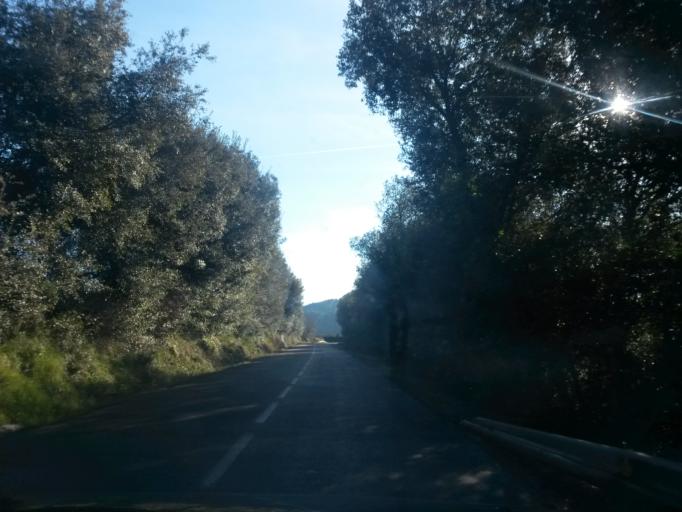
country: ES
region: Catalonia
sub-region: Provincia de Girona
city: Sant Gregori
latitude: 42.0237
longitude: 2.6772
